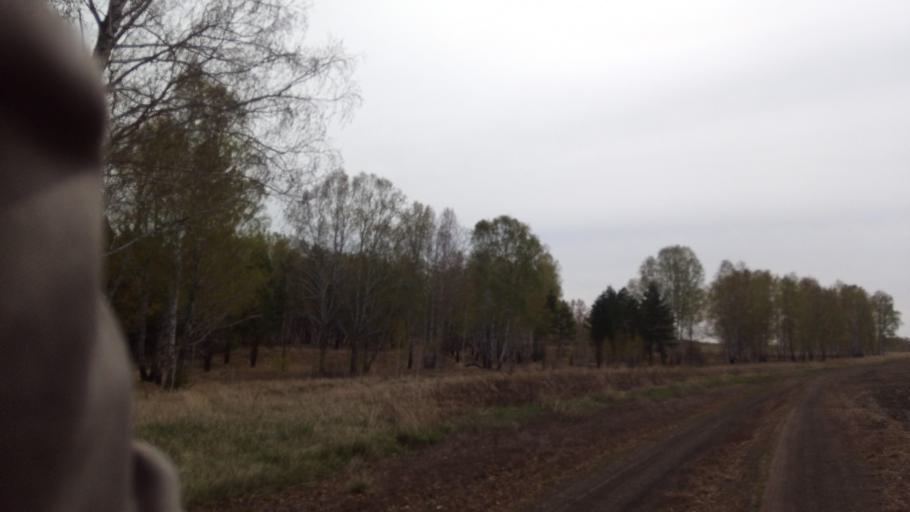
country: RU
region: Chelyabinsk
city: Timiryazevskiy
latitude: 55.0177
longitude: 60.8562
